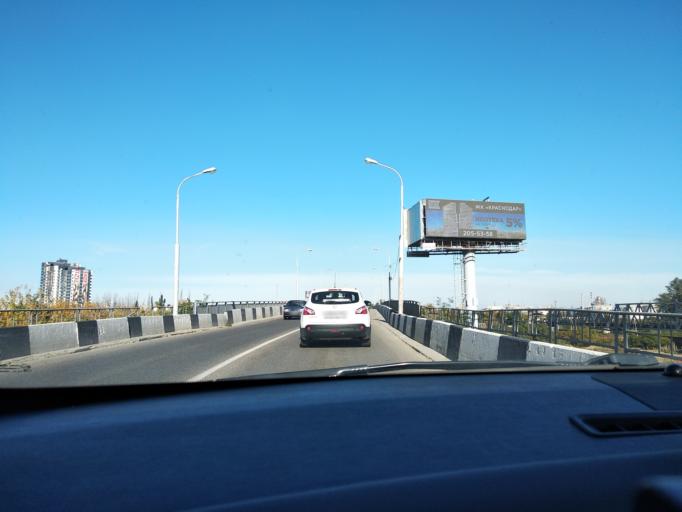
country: RU
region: Adygeya
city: Yablonovskiy
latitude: 44.9943
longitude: 38.9561
